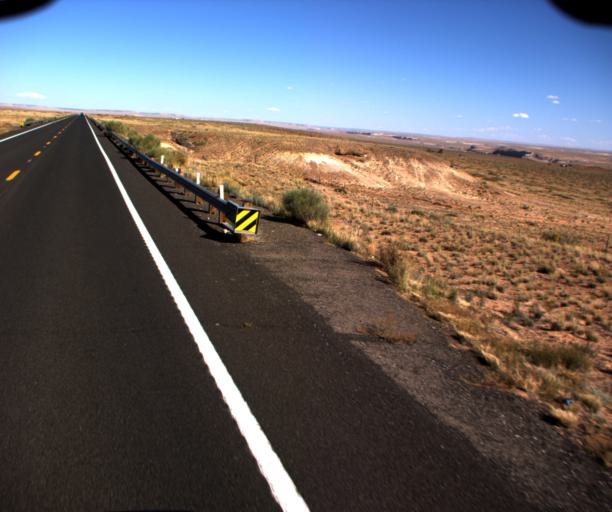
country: US
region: Arizona
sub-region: Coconino County
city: Tuba City
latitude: 36.1548
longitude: -111.1223
